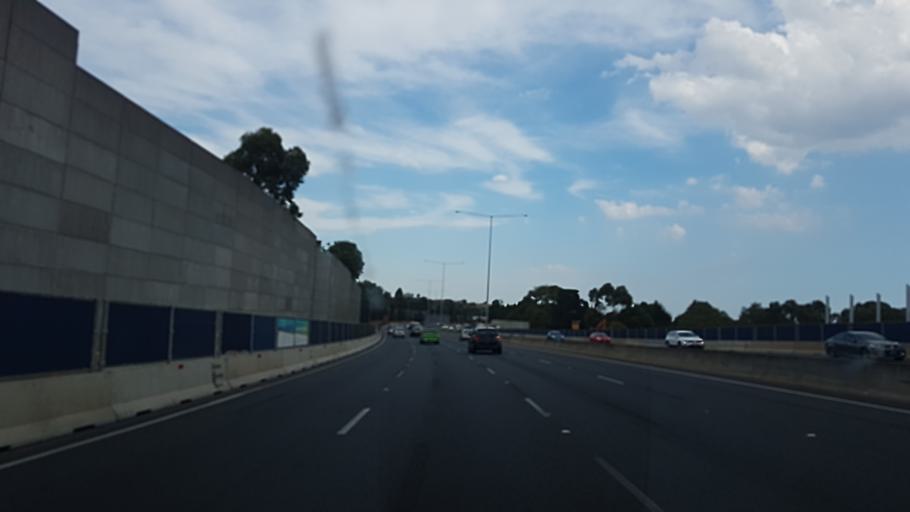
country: AU
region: Victoria
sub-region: Moreland
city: Pascoe Vale
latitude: -37.7407
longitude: 144.9315
